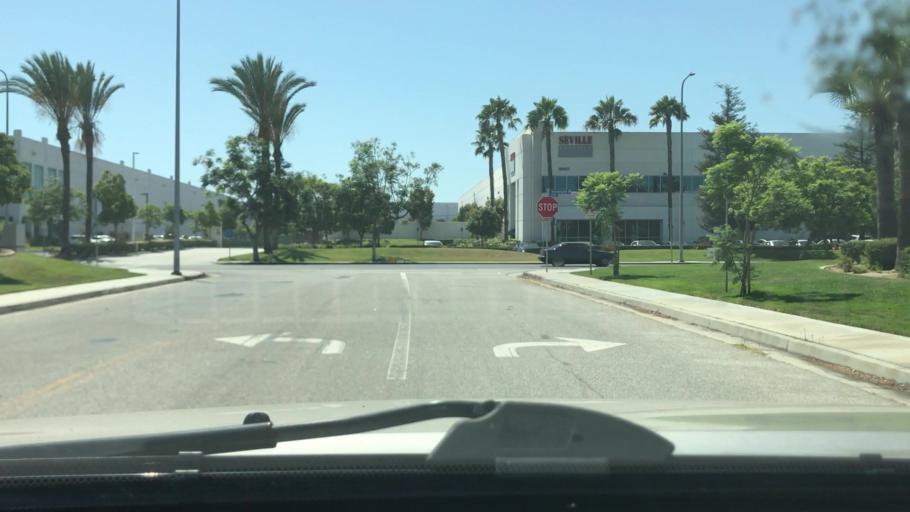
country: US
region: California
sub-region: Los Angeles County
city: Carson
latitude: 33.8543
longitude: -118.3030
